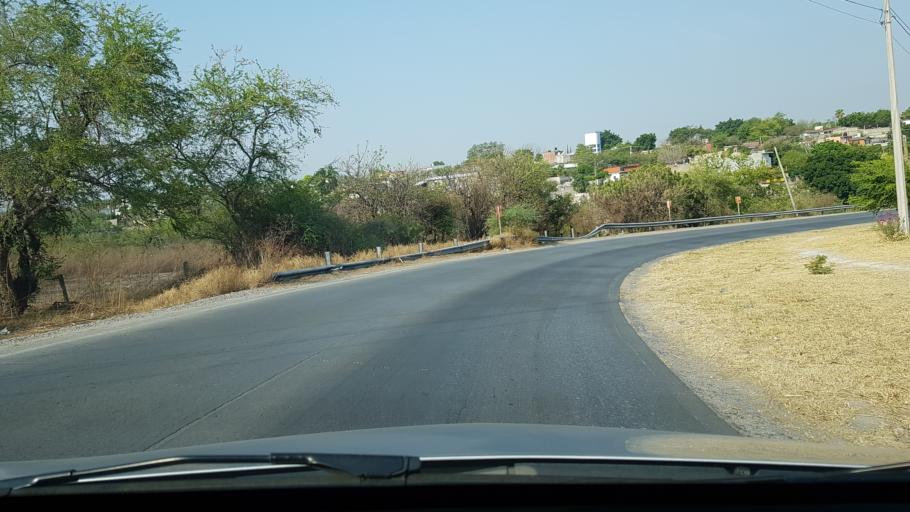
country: MX
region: Morelos
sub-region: Tlaquiltenango
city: Alfredo V. Bonfil (Chacampalco)
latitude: 18.6572
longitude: -99.1520
